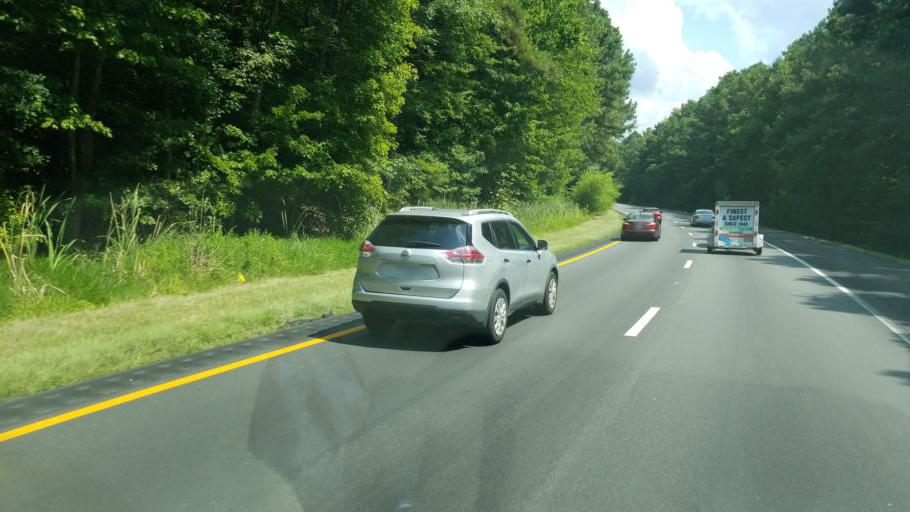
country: US
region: Virginia
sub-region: City of Suffolk
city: Suffolk
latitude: 36.7539
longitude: -76.5300
